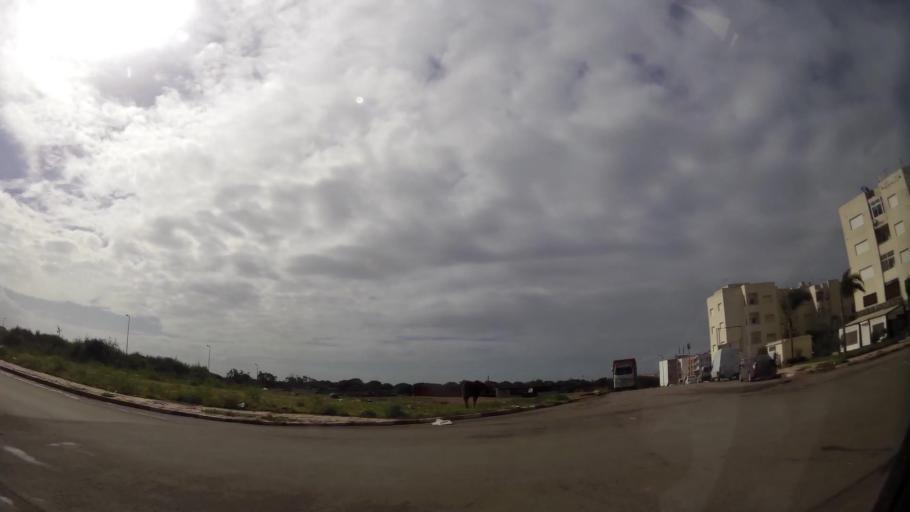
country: MA
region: Grand Casablanca
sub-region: Mohammedia
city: Mohammedia
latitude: 33.6713
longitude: -7.3953
